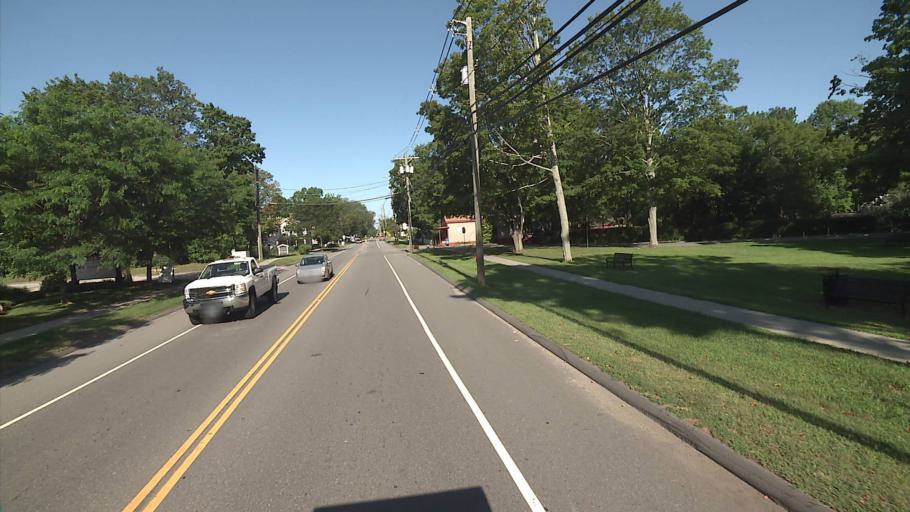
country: US
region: Connecticut
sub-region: Middlesex County
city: Clinton
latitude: 41.2768
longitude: -72.5174
